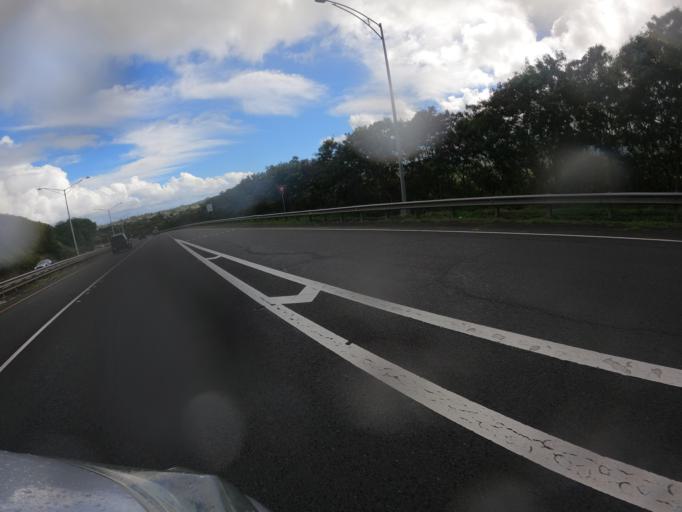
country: US
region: Hawaii
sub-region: Honolulu County
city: Kailua
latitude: 21.4054
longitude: -157.7650
